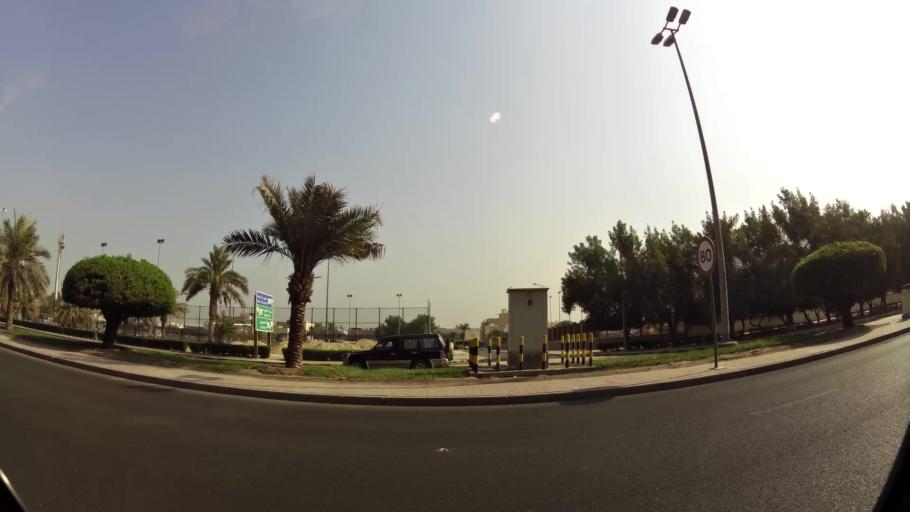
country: KW
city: Bayan
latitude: 29.3031
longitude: 48.0590
